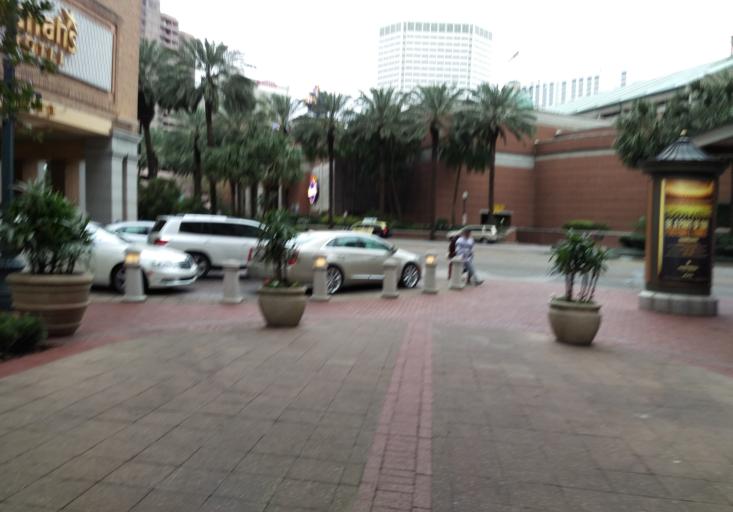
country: US
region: Louisiana
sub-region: Orleans Parish
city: New Orleans
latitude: 29.9480
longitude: -90.0655
